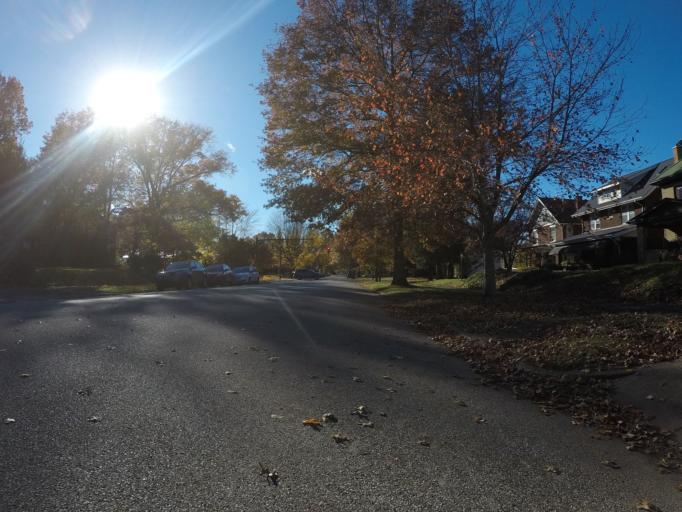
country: US
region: West Virginia
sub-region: Cabell County
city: Huntington
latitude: 38.4100
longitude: -82.4472
